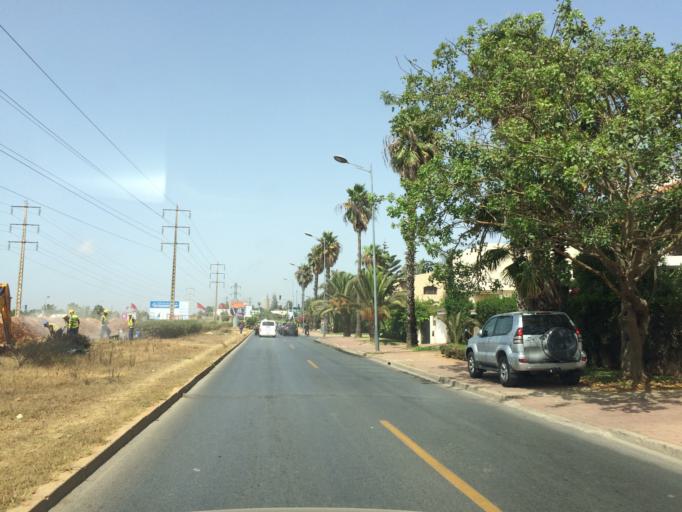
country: MA
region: Rabat-Sale-Zemmour-Zaer
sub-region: Skhirate-Temara
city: Temara
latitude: 33.9686
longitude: -6.8671
